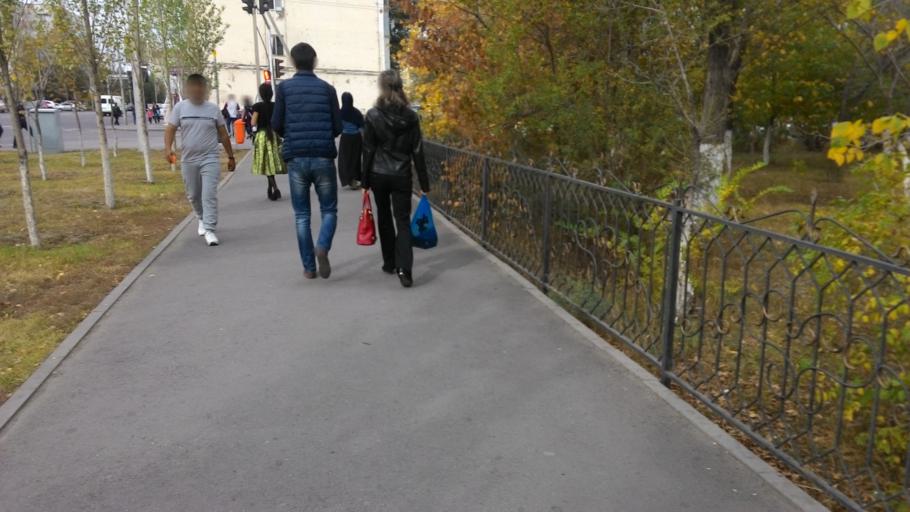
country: KZ
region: Astana Qalasy
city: Astana
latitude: 51.1876
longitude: 71.4081
